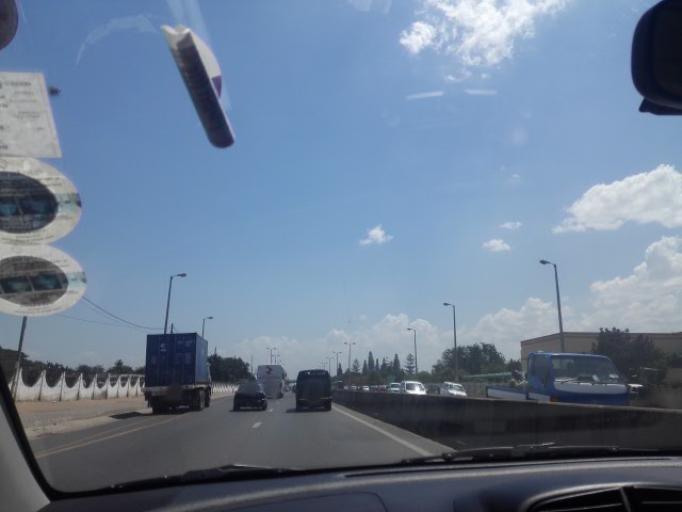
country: MZ
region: Maputo City
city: Maputo
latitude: -25.9363
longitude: 32.5488
